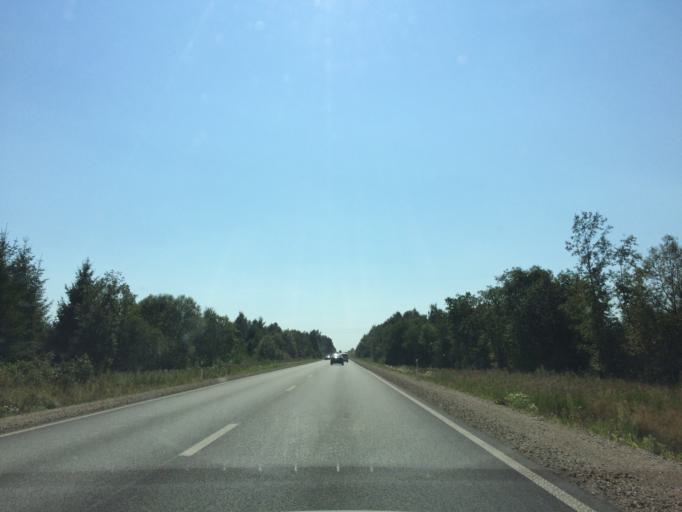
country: LV
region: Rezekne
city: Rezekne
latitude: 56.3878
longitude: 27.2085
